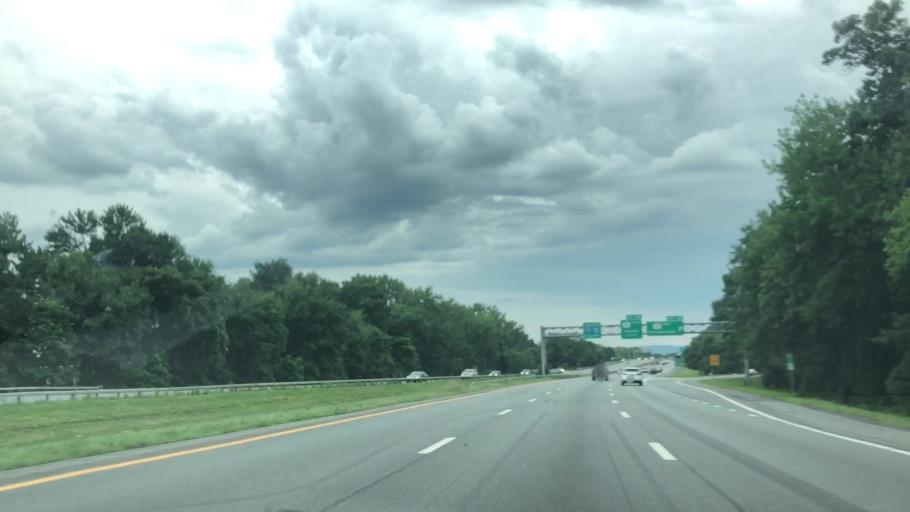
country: US
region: New York
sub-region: Albany County
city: Colonie
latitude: 42.7149
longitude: -73.8186
